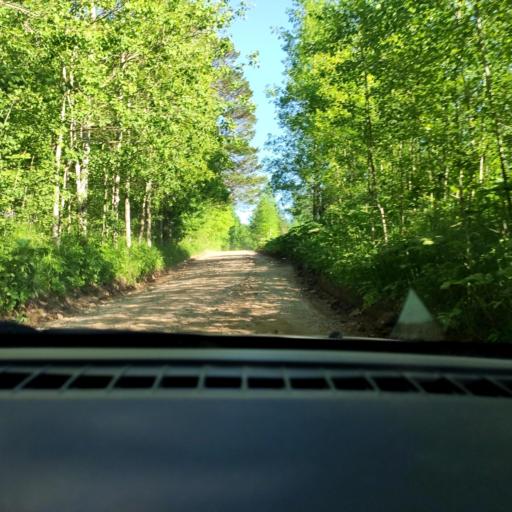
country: RU
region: Perm
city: Overyata
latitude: 58.1257
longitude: 55.8769
